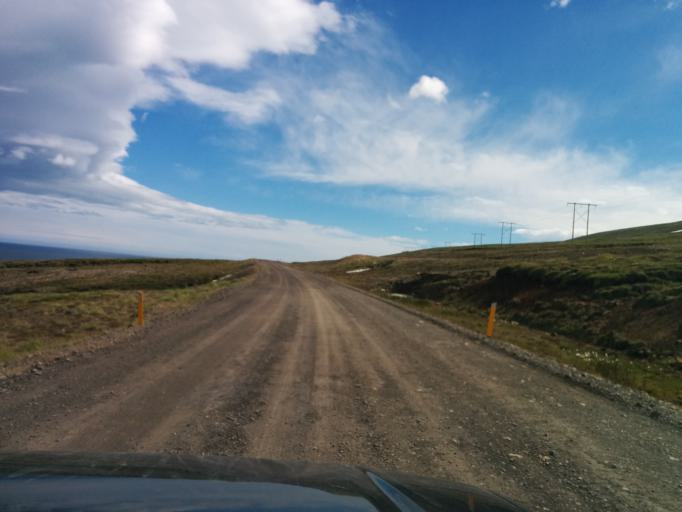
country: IS
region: East
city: Egilsstadir
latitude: 65.7474
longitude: -14.6532
